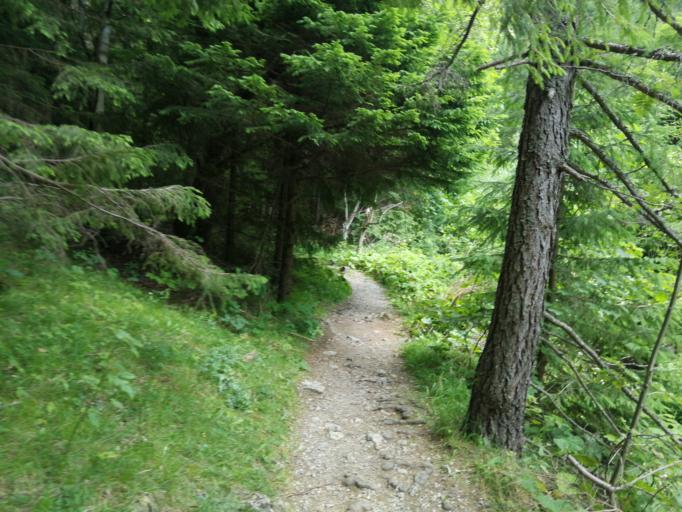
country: SK
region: Zilinsky
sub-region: Okres Liptovsky Mikulas
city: Liptovsky Mikulas
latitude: 49.1761
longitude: 19.4867
